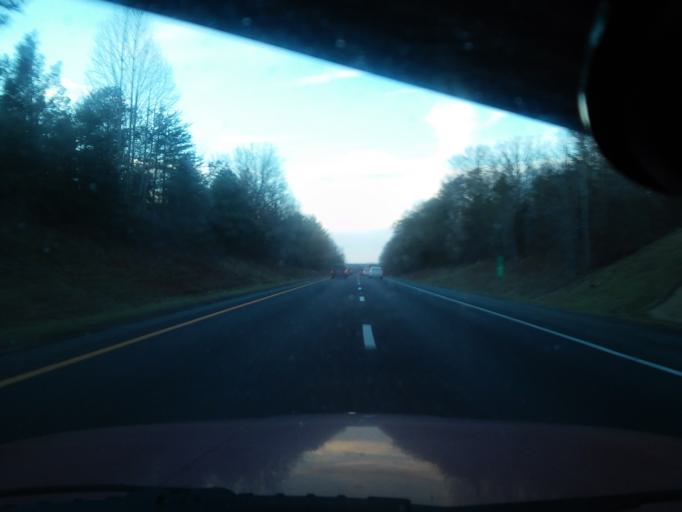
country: US
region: Virginia
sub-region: Louisa County
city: Louisa
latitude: 37.9053
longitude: -78.0554
